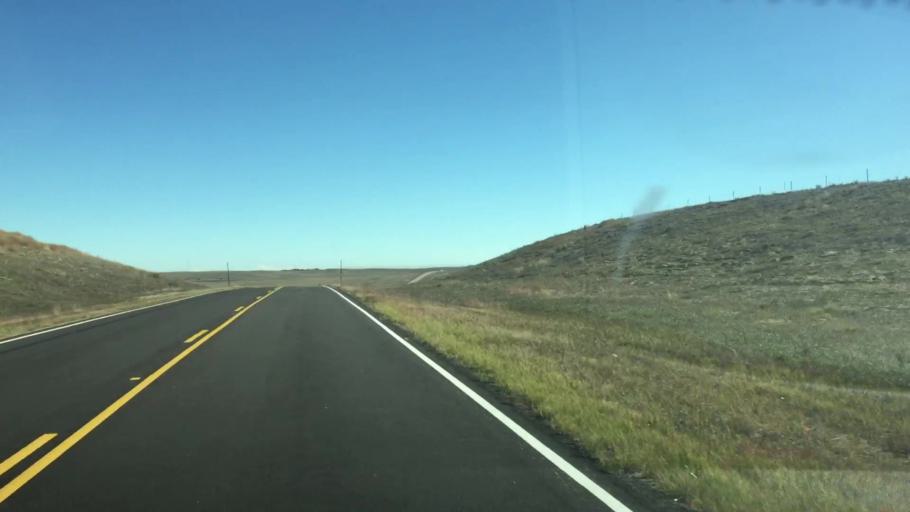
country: US
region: Colorado
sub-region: Lincoln County
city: Limon
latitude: 39.3026
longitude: -103.8457
